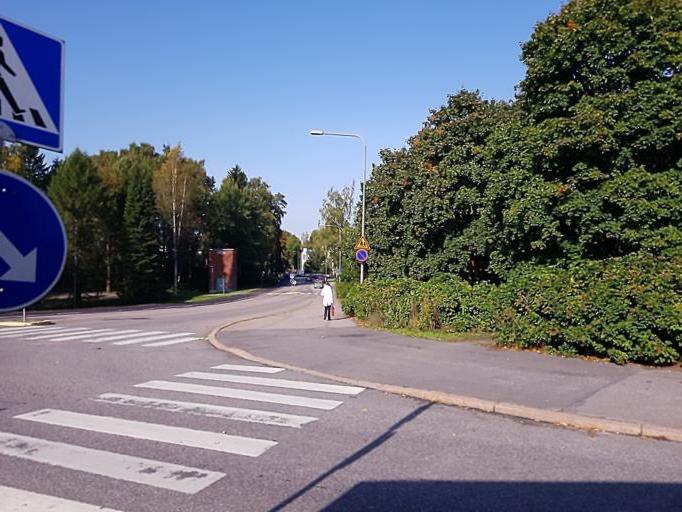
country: FI
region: Uusimaa
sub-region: Helsinki
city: Teekkarikylae
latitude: 60.2431
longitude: 24.8855
